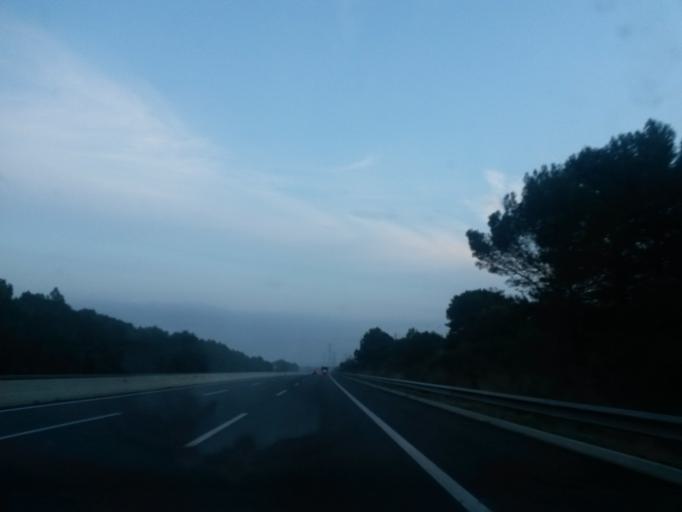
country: ES
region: Catalonia
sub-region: Provincia de Girona
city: Garrigas
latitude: 42.2008
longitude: 2.9352
